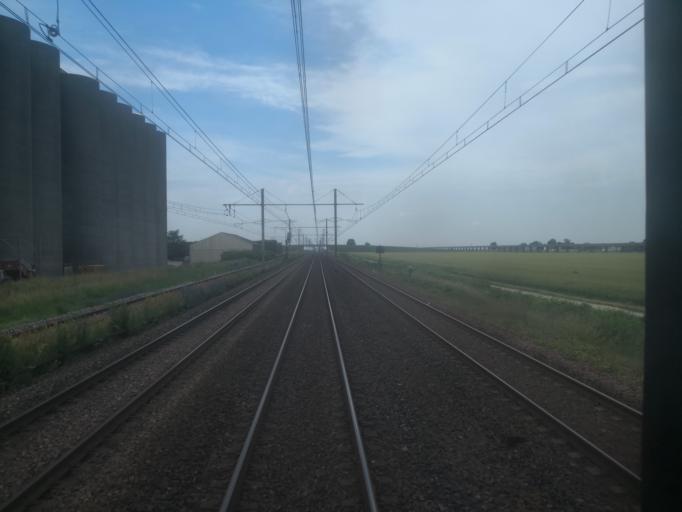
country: FR
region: Centre
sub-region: Departement du Loiret
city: Artenay
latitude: 48.0911
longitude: 1.8873
